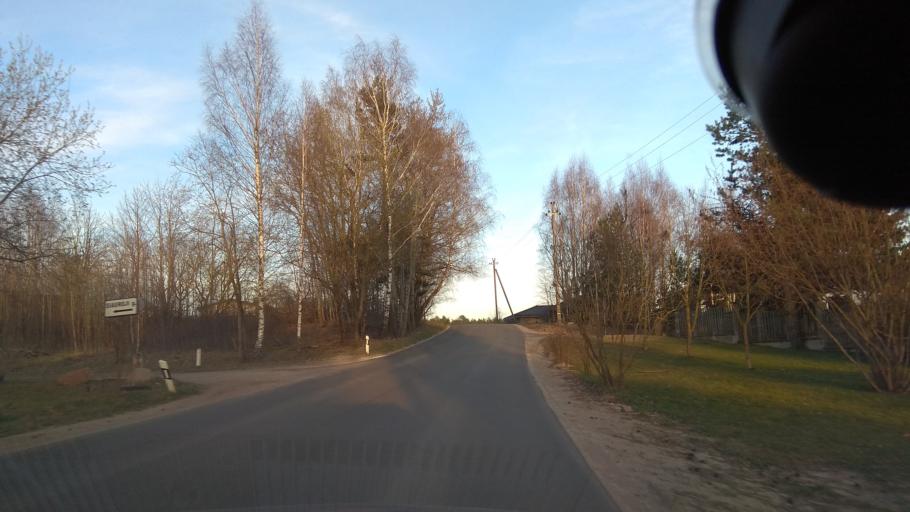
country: LT
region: Vilnius County
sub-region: Vilnius
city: Fabijoniskes
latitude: 54.7573
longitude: 25.2330
